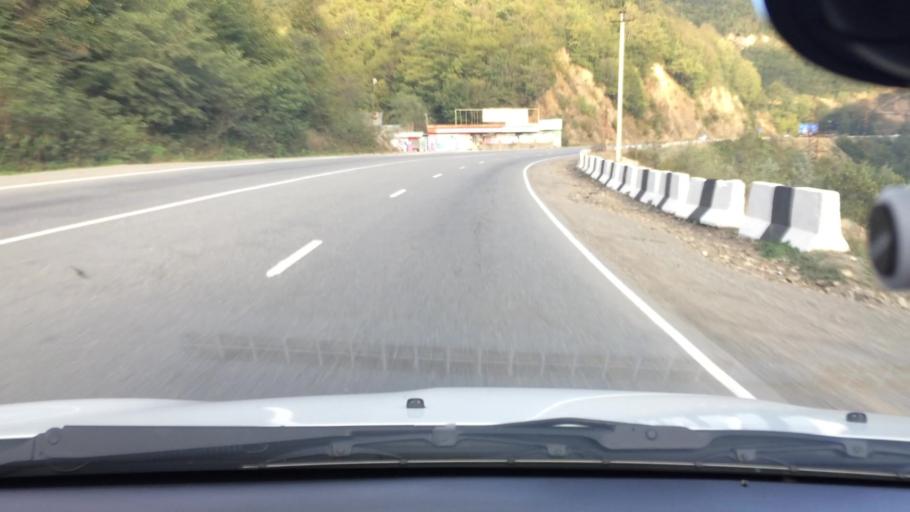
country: GE
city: Surami
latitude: 42.0421
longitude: 43.5017
